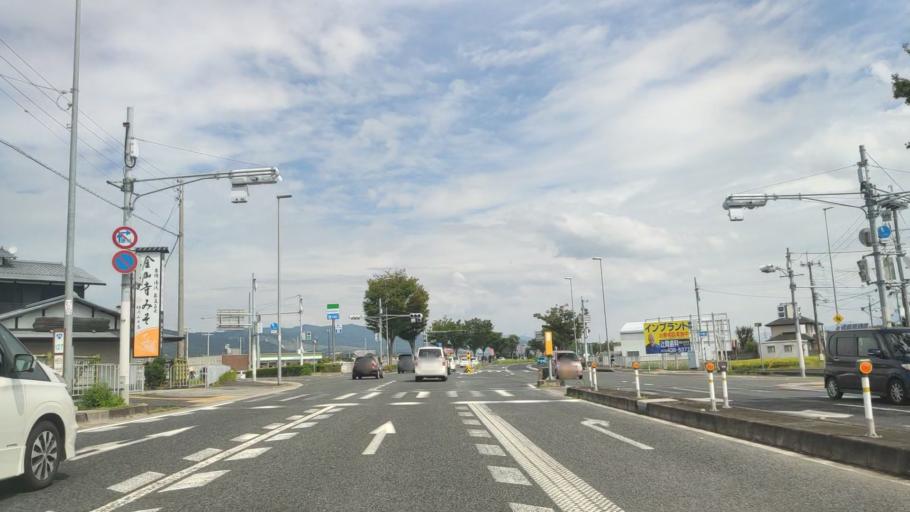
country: JP
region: Wakayama
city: Iwade
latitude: 34.2630
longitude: 135.2676
